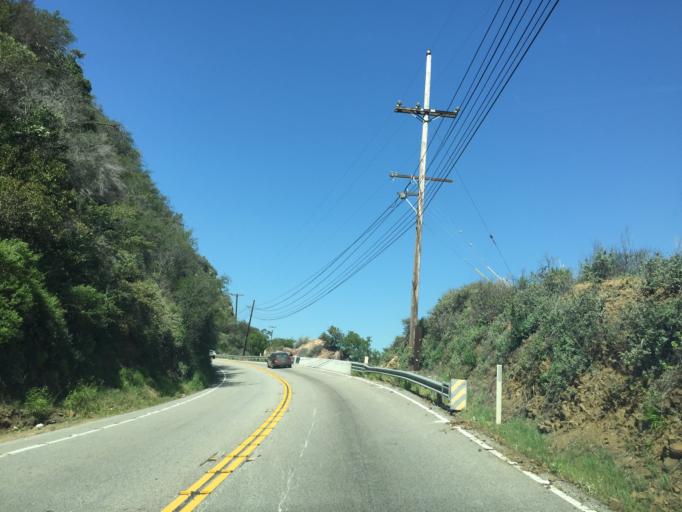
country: US
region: California
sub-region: Los Angeles County
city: Topanga
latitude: 34.0763
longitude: -118.5915
